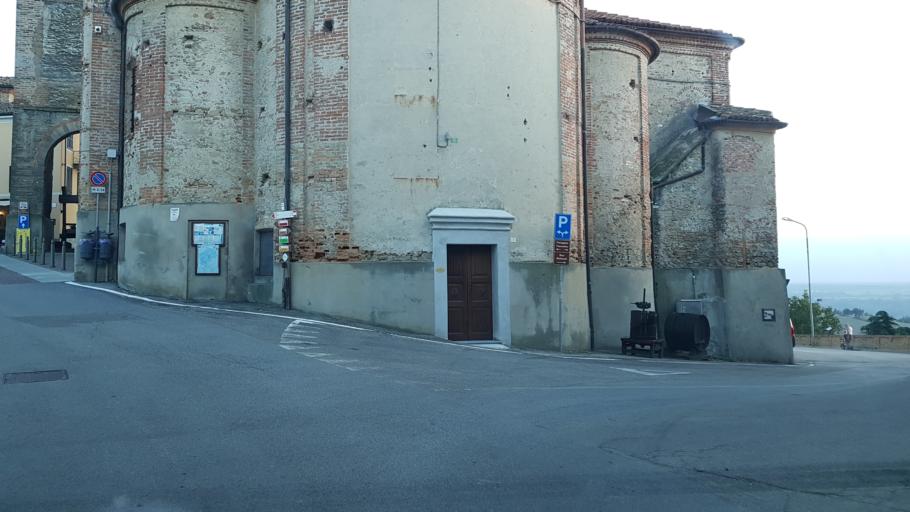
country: IT
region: Piedmont
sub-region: Provincia di Cuneo
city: Novello
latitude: 44.5889
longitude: 7.9274
